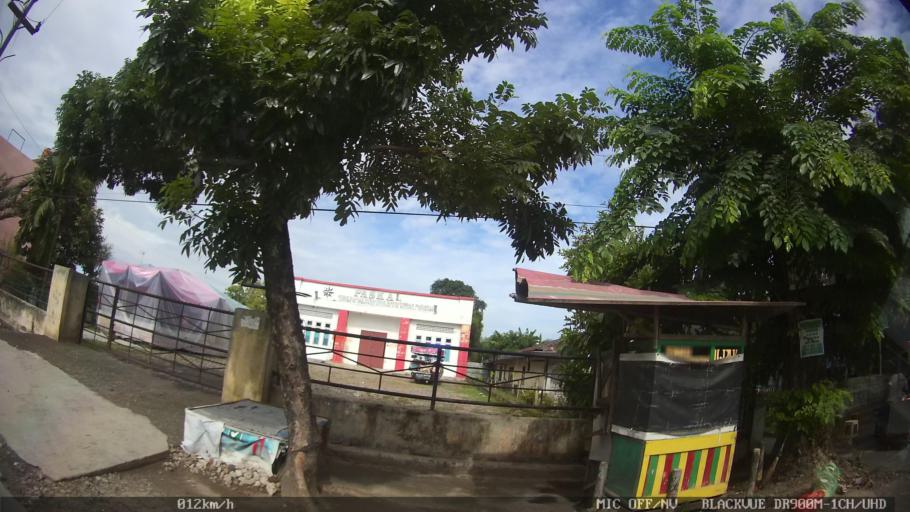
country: ID
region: North Sumatra
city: Sunggal
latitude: 3.6066
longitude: 98.6121
